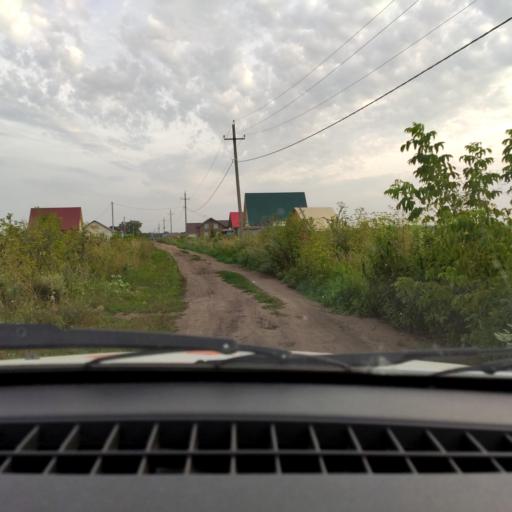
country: RU
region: Bashkortostan
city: Blagoveshchensk
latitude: 54.9271
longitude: 55.9728
